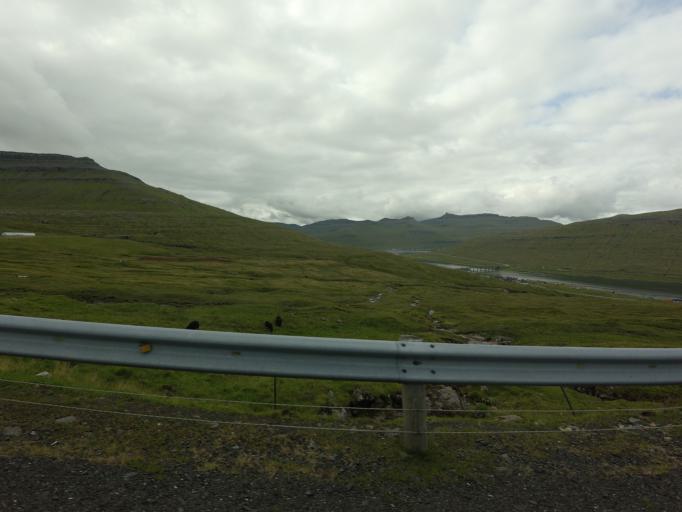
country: FO
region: Eysturoy
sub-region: Eidi
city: Eidi
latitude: 62.2212
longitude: -6.9876
